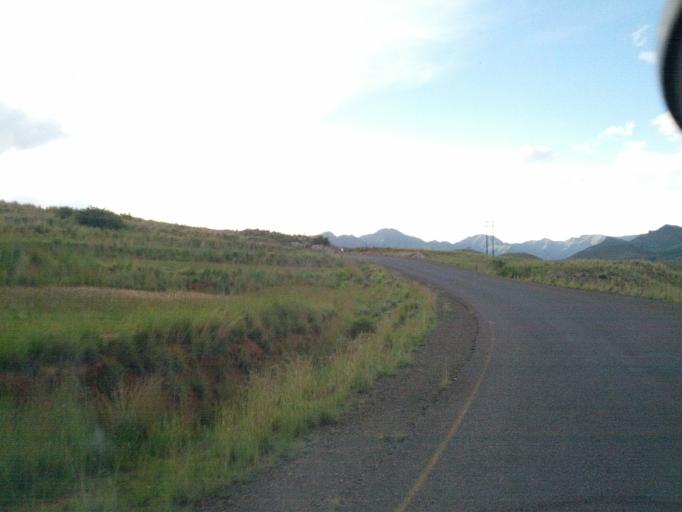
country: LS
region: Qacha's Nek
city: Qacha's Nek
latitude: -30.0738
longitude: 28.5790
